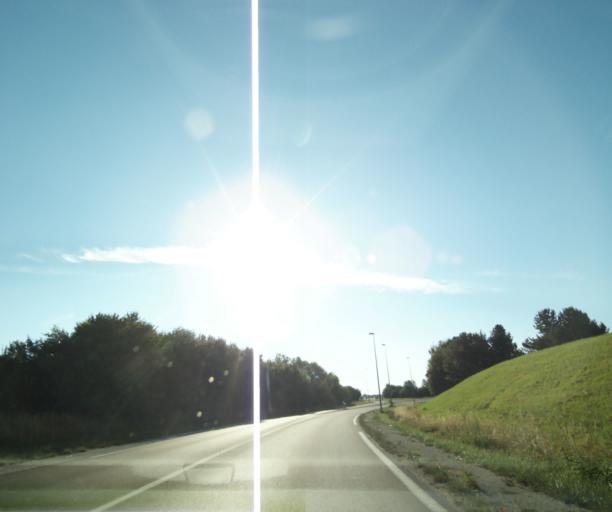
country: FR
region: Ile-de-France
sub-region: Departement de Seine-et-Marne
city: Marolles-sur-Seine
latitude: 48.3840
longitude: 3.0165
